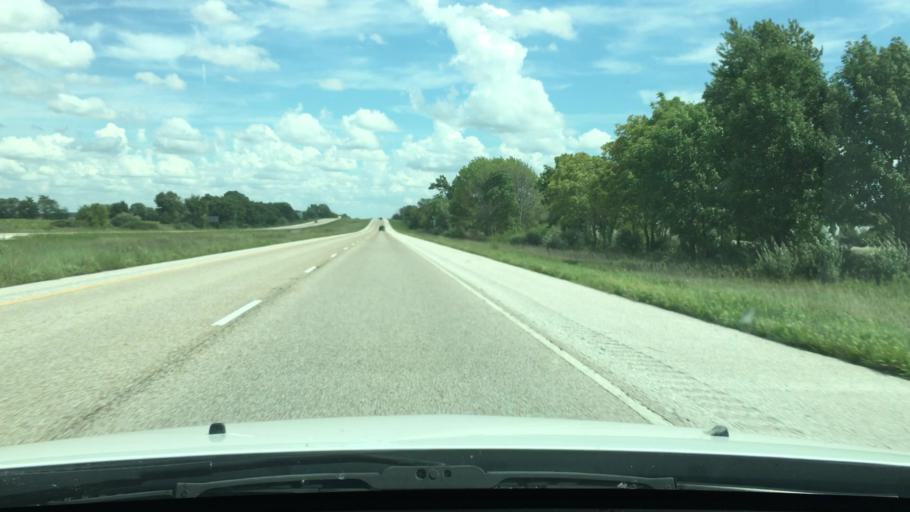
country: US
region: Illinois
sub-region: Scott County
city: Winchester
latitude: 39.6810
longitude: -90.4390
